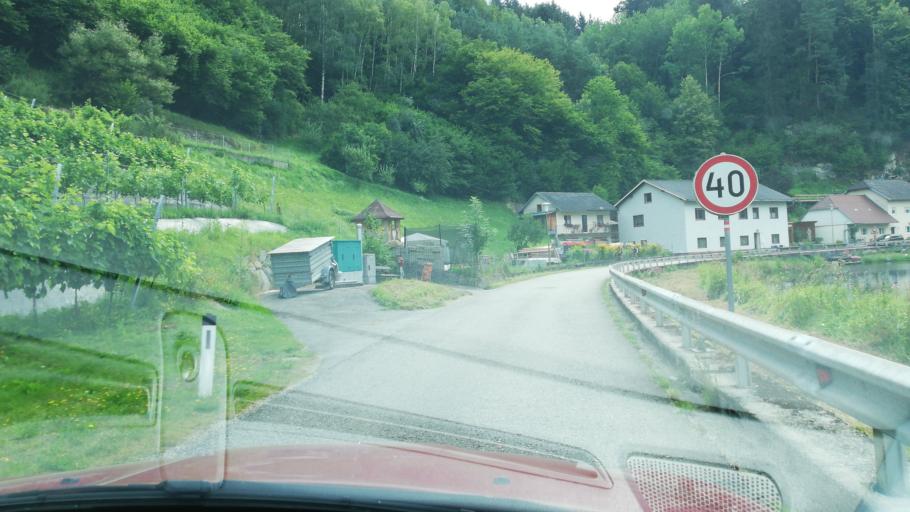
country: AT
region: Upper Austria
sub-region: Politischer Bezirk Rohrbach
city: Kleinzell im Muehlkreis
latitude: 48.5044
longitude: 14.0114
